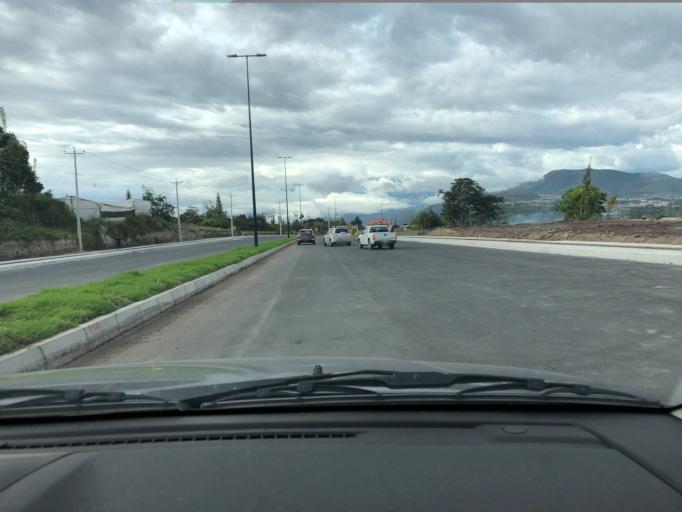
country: EC
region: Imbabura
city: Ibarra
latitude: 0.3373
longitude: -78.1570
